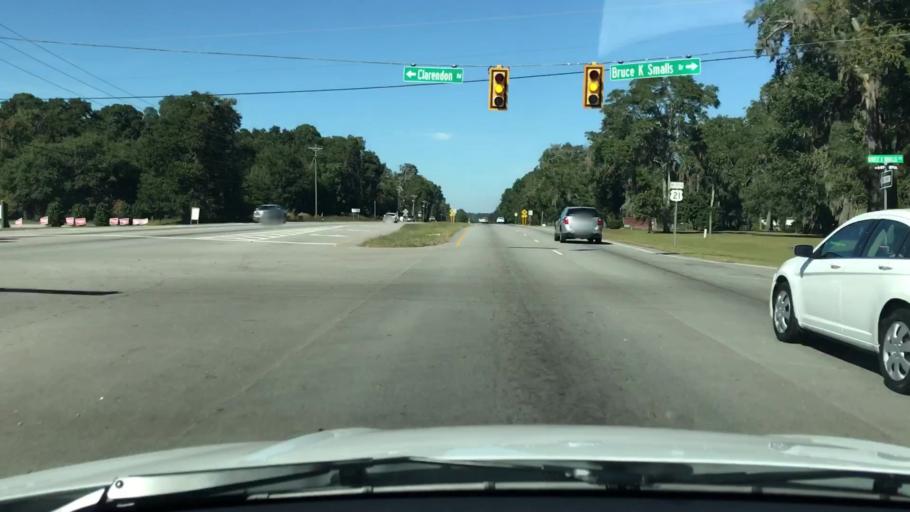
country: US
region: South Carolina
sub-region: Beaufort County
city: Burton
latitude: 32.4931
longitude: -80.7422
